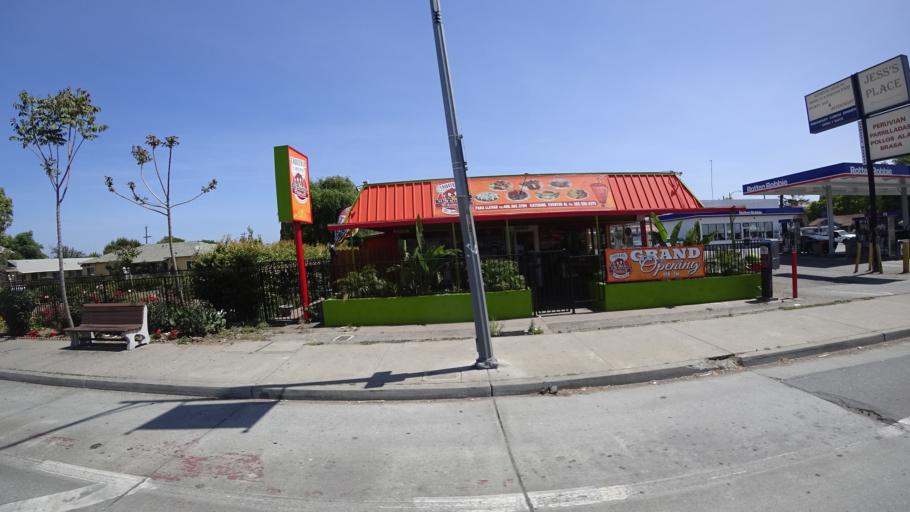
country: US
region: California
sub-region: Santa Clara County
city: Seven Trees
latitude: 37.2880
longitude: -121.8454
